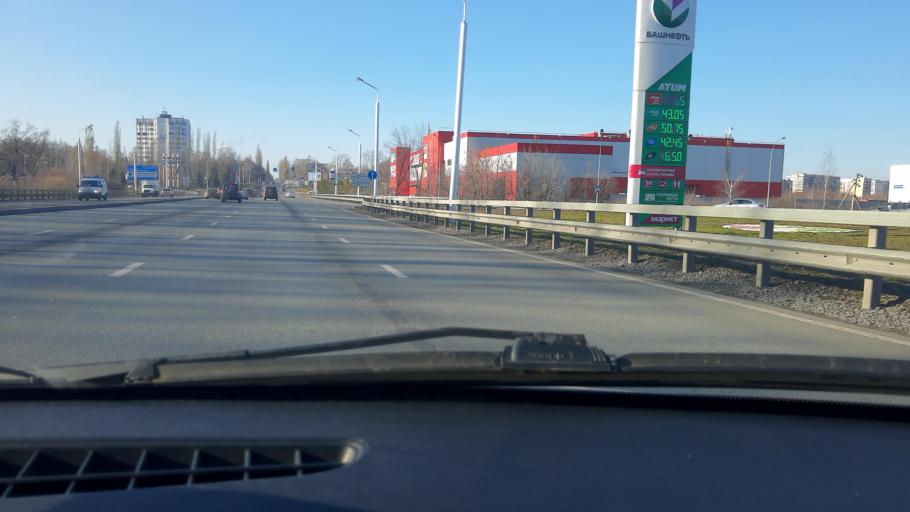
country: RU
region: Bashkortostan
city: Mikhaylovka
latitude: 54.7057
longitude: 55.8504
